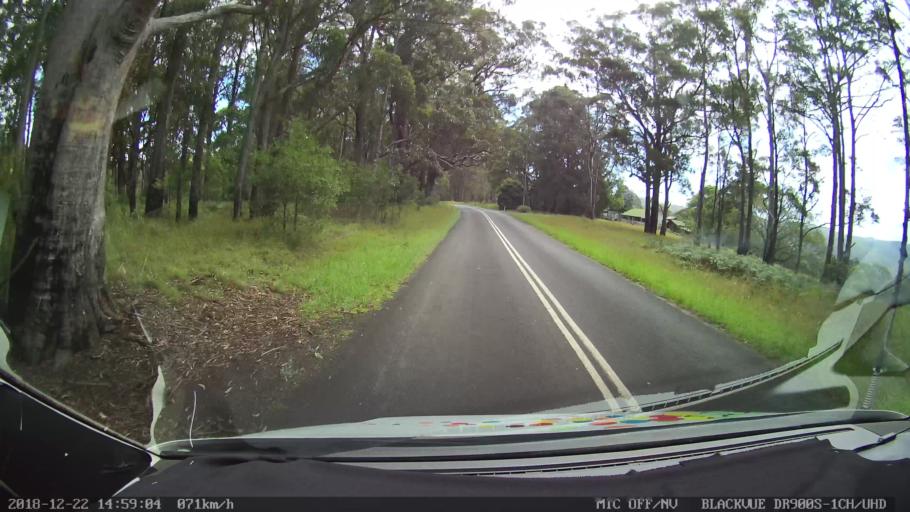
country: AU
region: New South Wales
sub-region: Bellingen
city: Dorrigo
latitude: -30.2440
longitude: 152.4848
